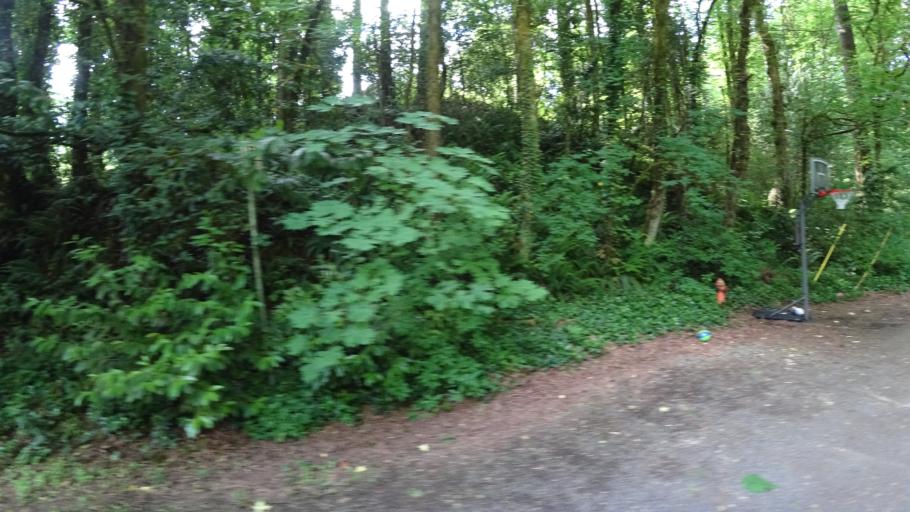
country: US
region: Oregon
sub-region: Multnomah County
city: Portland
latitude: 45.5057
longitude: -122.7087
